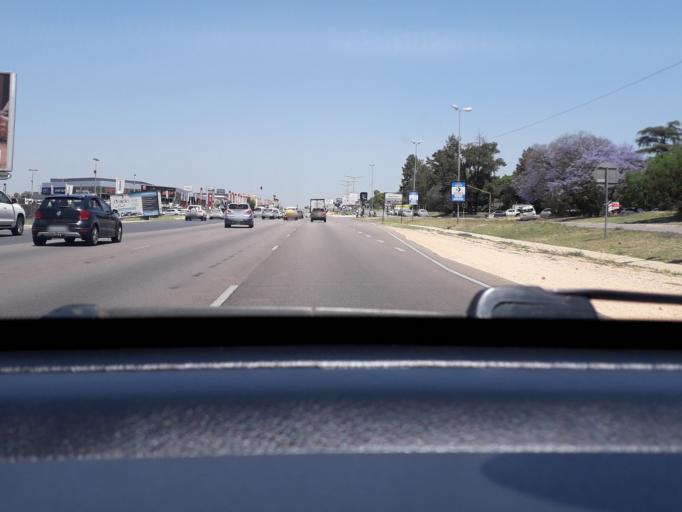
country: ZA
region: Gauteng
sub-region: City of Johannesburg Metropolitan Municipality
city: Midrand
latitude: -26.0483
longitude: 28.0906
